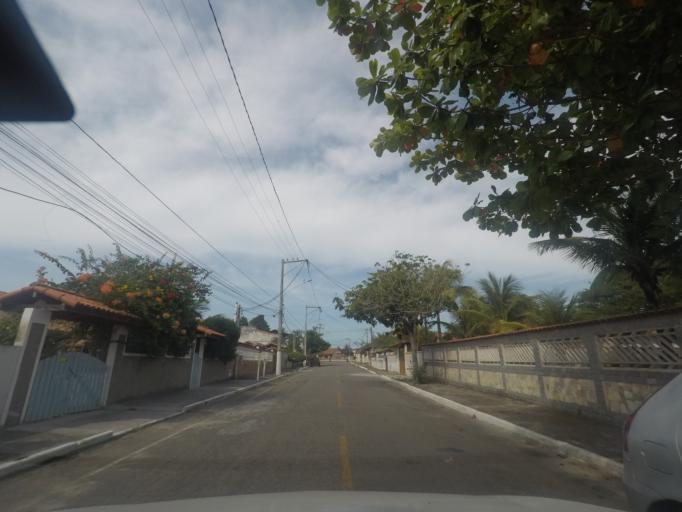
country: BR
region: Rio de Janeiro
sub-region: Marica
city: Marica
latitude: -22.9569
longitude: -42.8135
